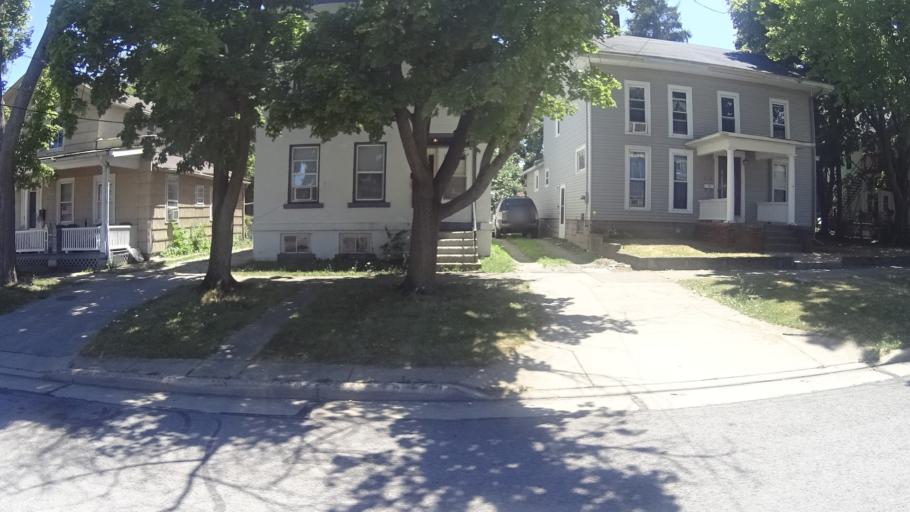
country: US
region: Ohio
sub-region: Erie County
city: Sandusky
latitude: 41.4556
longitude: -82.7044
